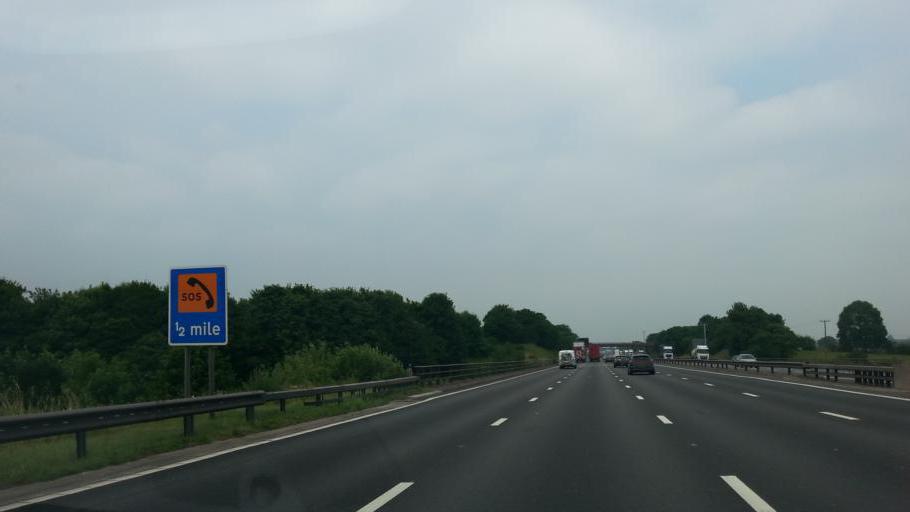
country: GB
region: England
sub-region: Staffordshire
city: Penkridge
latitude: 52.7391
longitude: -2.0988
